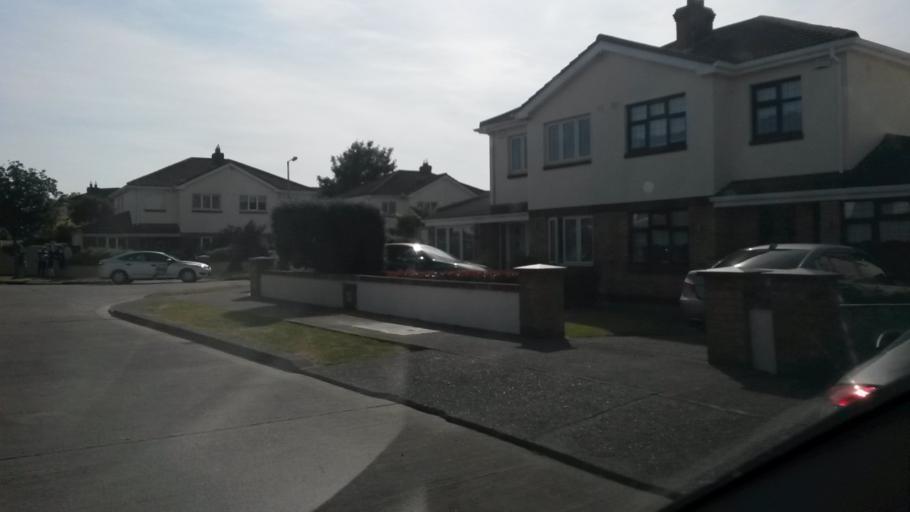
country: IE
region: Leinster
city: Lusk
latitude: 53.5239
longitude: -6.1647
